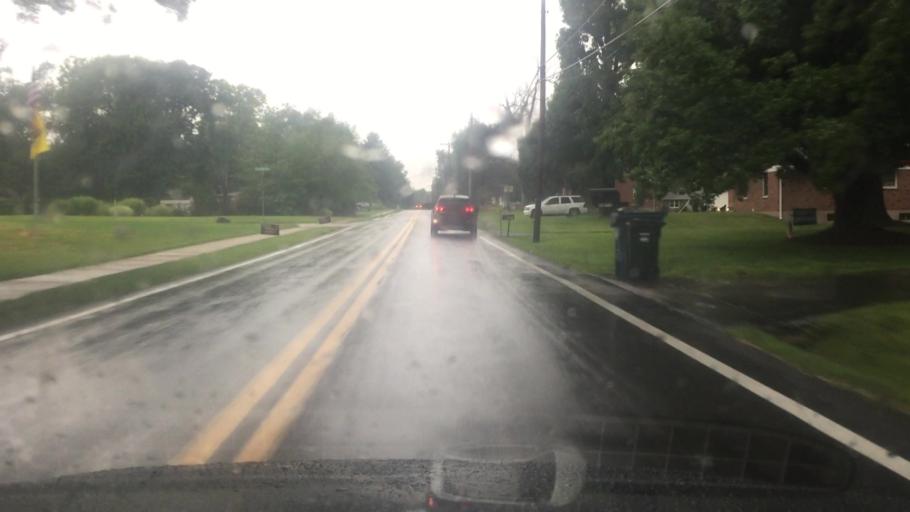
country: US
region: Missouri
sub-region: Saint Louis County
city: Concord
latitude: 38.5151
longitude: -90.3595
